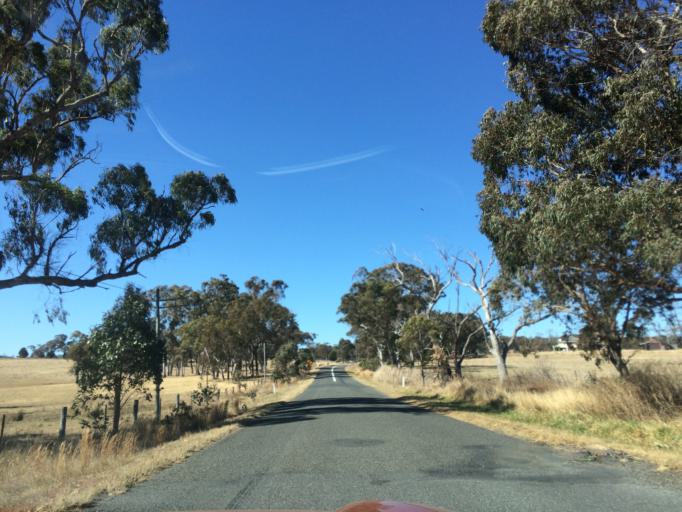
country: AU
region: Queensland
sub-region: Southern Downs
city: Stanthorpe
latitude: -28.6958
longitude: 152.0112
